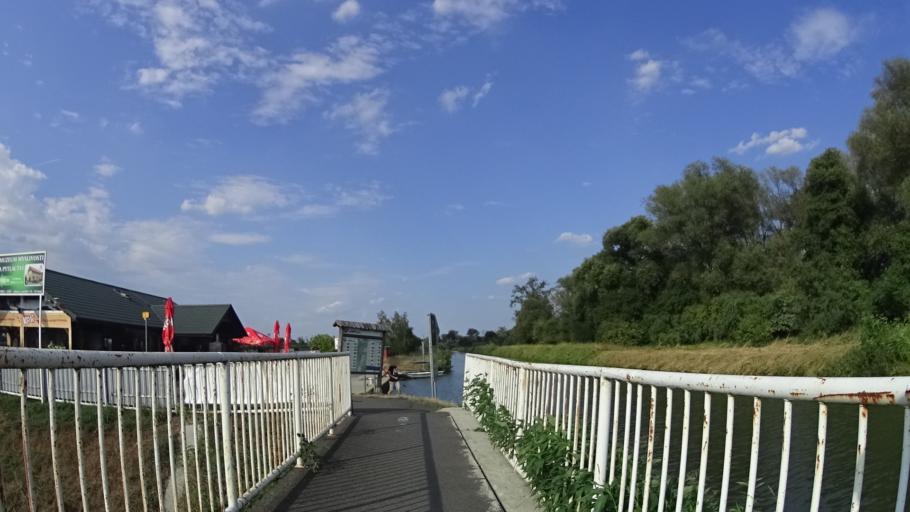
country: CZ
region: Zlin
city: Babice
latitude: 49.1166
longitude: 17.4845
